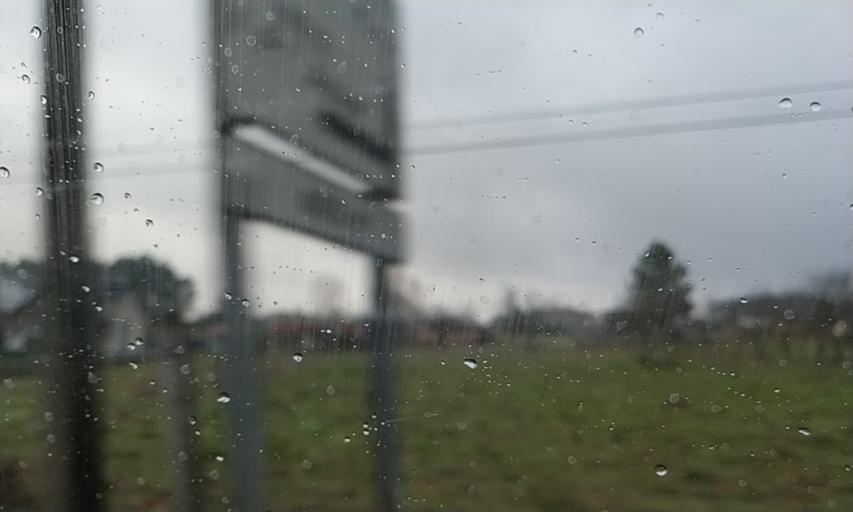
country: PT
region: Vila Real
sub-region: Murca
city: Murca
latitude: 41.3961
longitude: -7.4910
